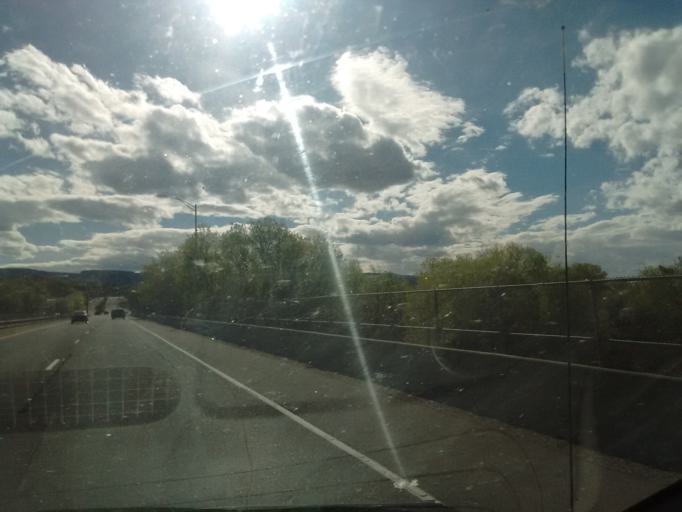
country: US
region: Colorado
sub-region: Mesa County
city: Grand Junction
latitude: 39.0675
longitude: -108.5816
